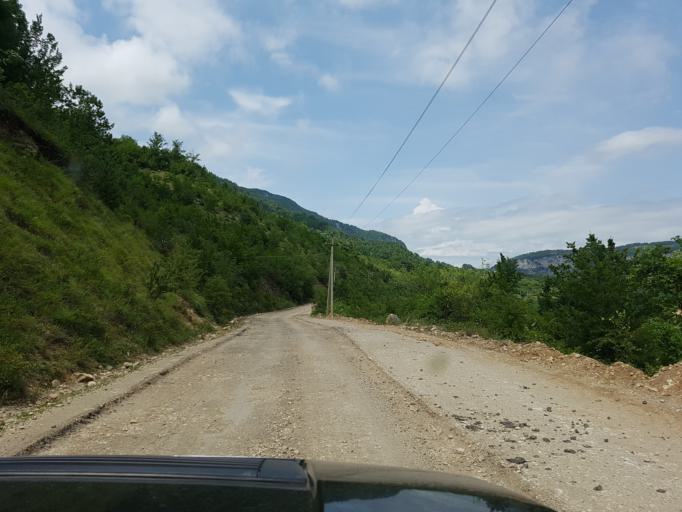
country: GE
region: Imereti
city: Tsqaltubo
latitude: 42.4950
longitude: 42.7842
